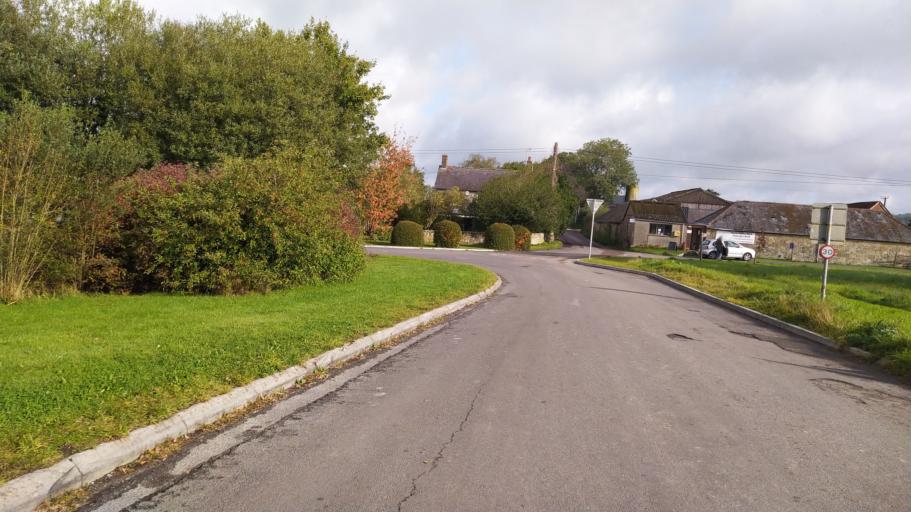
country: GB
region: England
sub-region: Dorset
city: Shaftesbury
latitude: 51.0416
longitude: -2.1558
